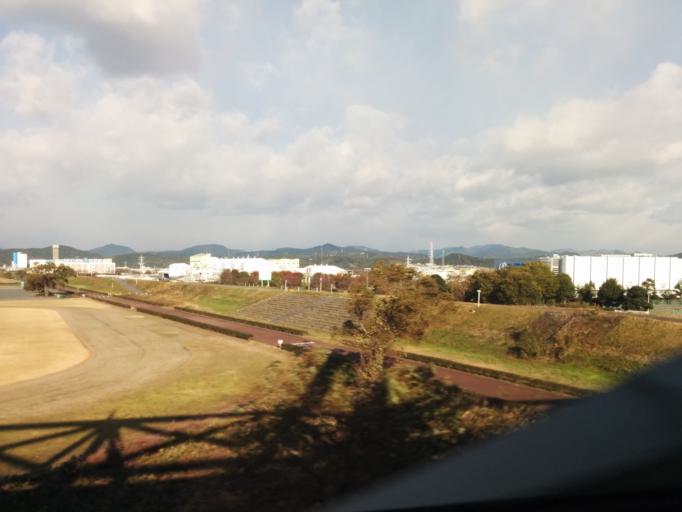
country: JP
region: Shizuoka
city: Shimada
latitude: 34.8220
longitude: 138.2329
